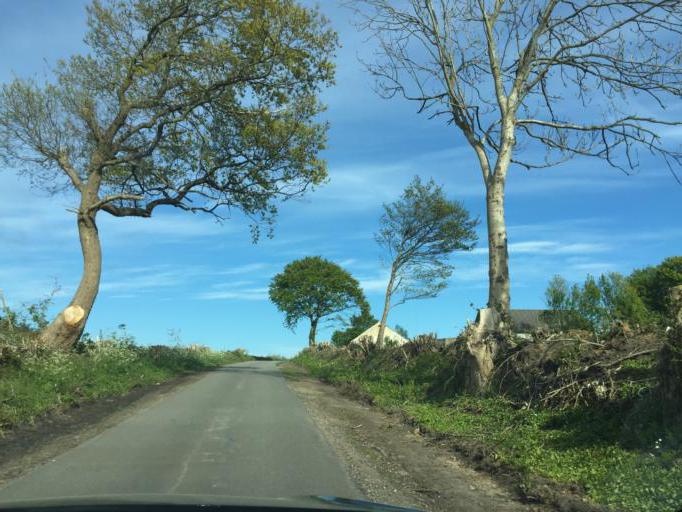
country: DK
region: South Denmark
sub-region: Fredericia Kommune
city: Taulov
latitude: 55.5265
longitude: 9.5448
